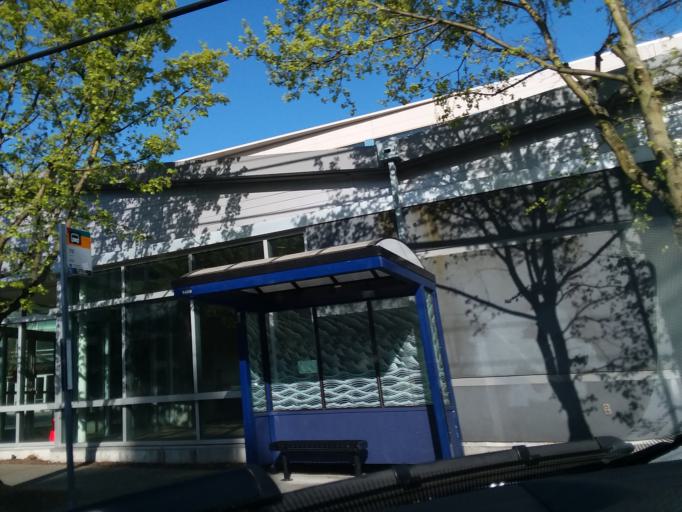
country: US
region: Washington
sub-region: King County
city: Seattle
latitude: 47.6342
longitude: -122.3254
